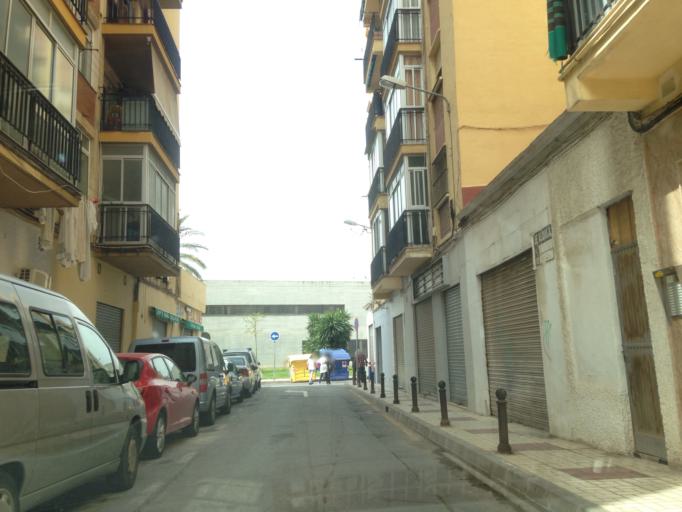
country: ES
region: Andalusia
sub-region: Provincia de Malaga
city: Malaga
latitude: 36.7112
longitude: -4.4374
